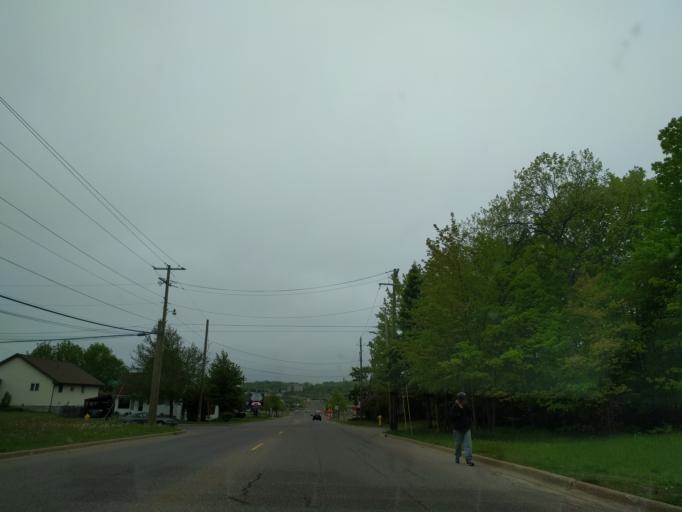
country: US
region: Michigan
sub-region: Marquette County
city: Trowbridge Park
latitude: 46.5493
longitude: -87.4199
